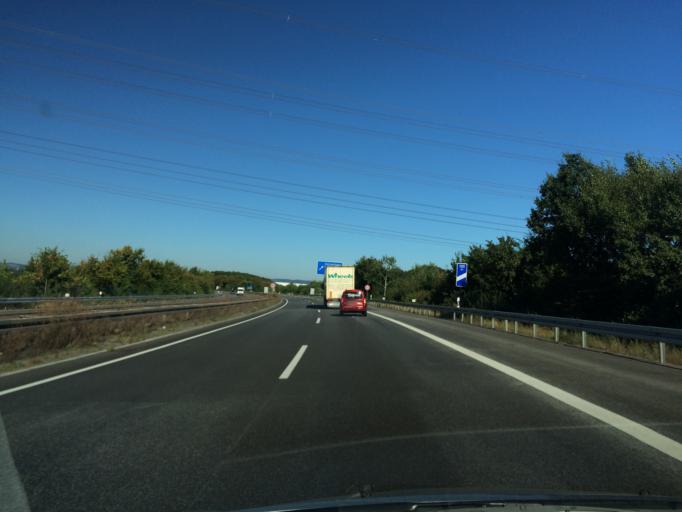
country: DE
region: Saarland
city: Saarwellingen
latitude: 49.3402
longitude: 6.8010
